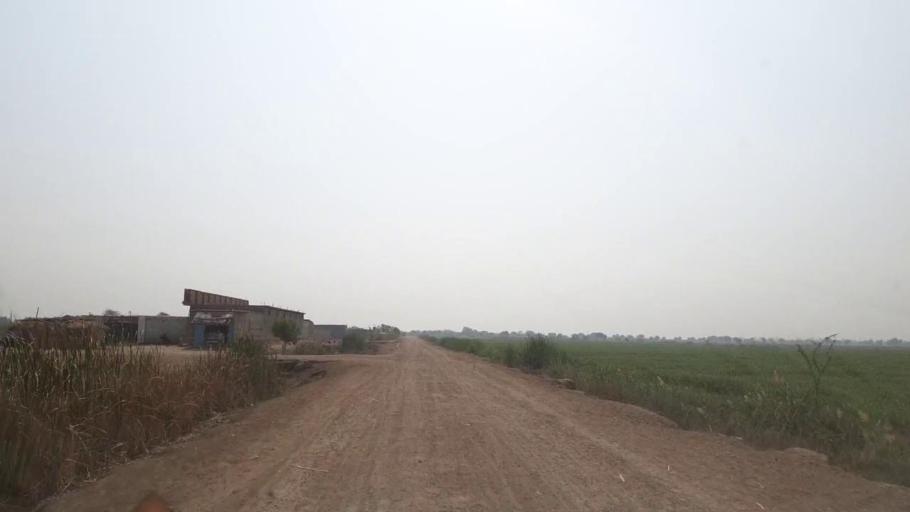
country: PK
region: Sindh
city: Mirpur Khas
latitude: 25.5410
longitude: 69.0614
